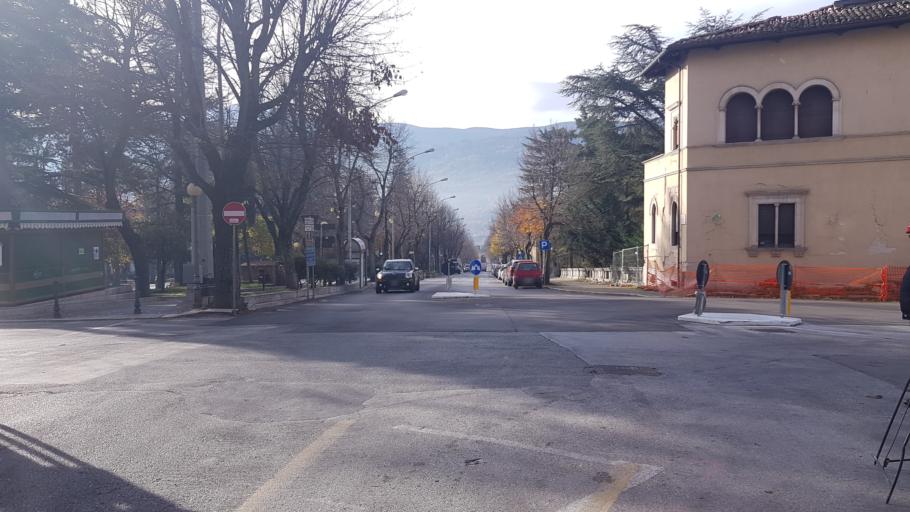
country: IT
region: Abruzzo
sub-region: Provincia dell' Aquila
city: L'Aquila
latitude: 42.3461
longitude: 13.3975
